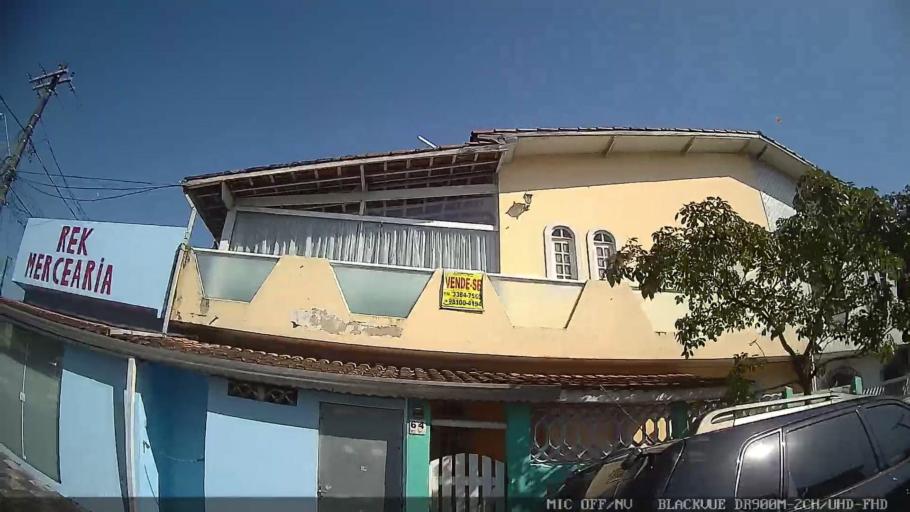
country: BR
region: Sao Paulo
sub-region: Santos
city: Santos
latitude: -23.9430
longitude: -46.2964
